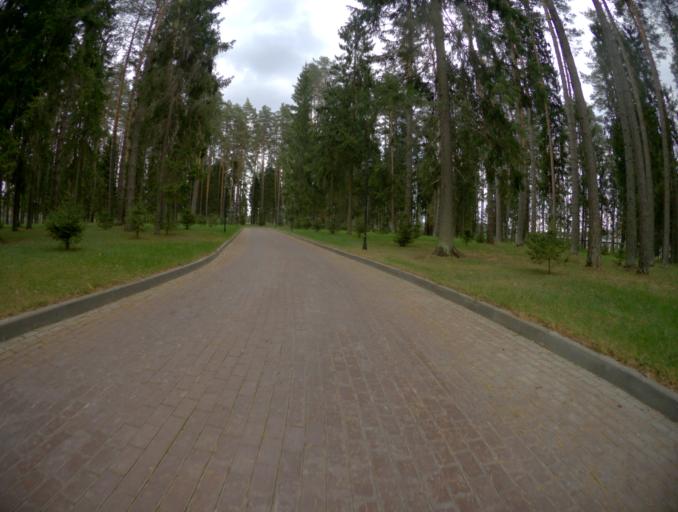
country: RU
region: Vladimir
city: Kideksha
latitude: 56.4759
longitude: 40.6719
